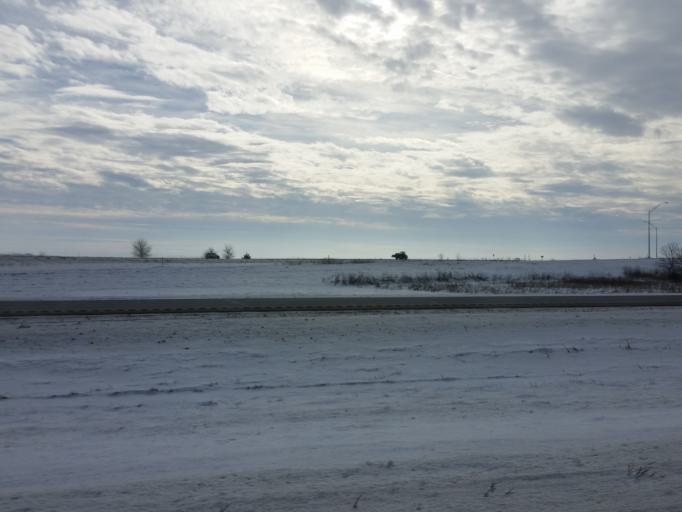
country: US
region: Iowa
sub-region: Buchanan County
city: Independence
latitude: 42.4483
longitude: -91.9173
